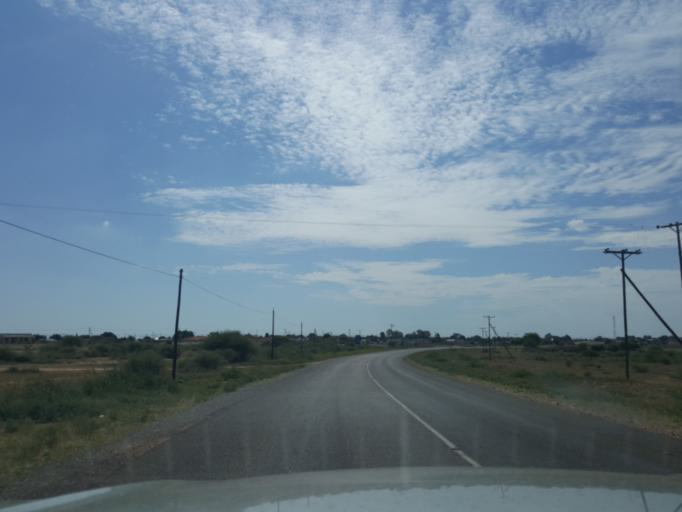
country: BW
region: Kweneng
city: Letlhakeng
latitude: -24.1148
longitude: 25.0380
